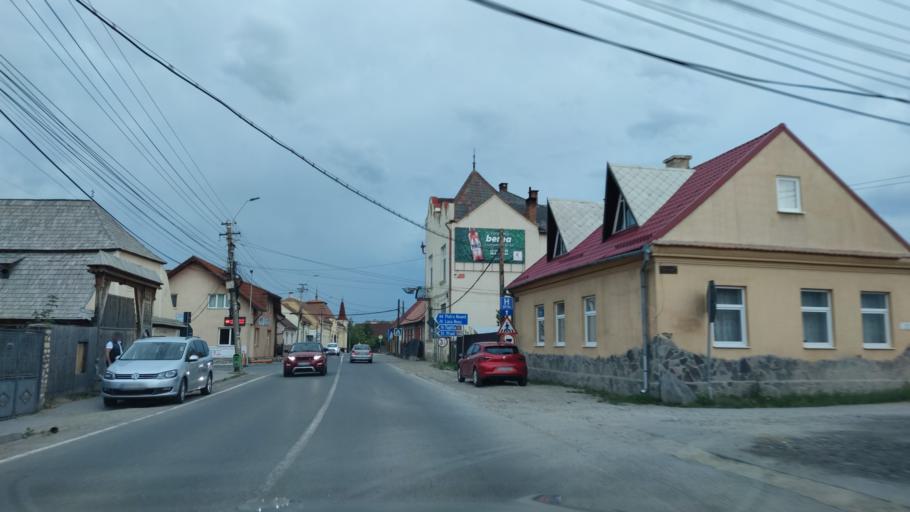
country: RO
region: Harghita
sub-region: Municipiul Gheorgheni
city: Gheorgheni
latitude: 46.7178
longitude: 25.6030
